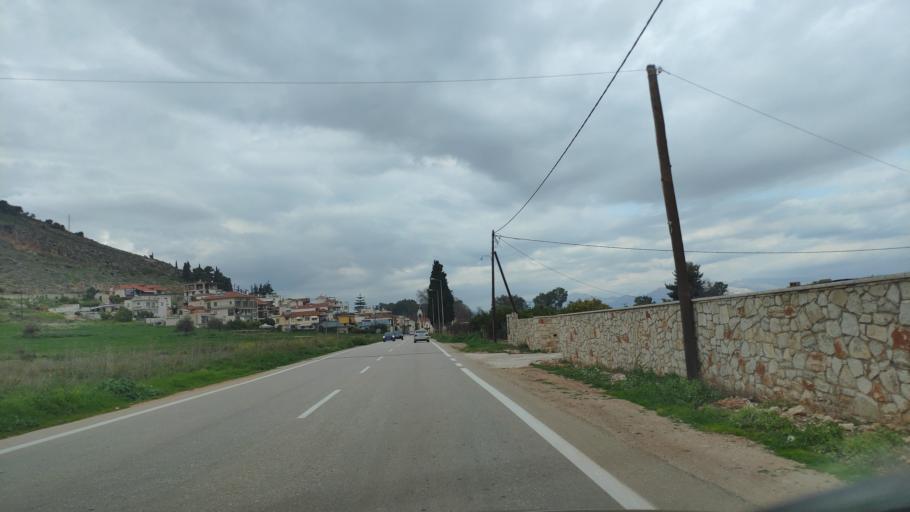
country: GR
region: Peloponnese
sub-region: Nomos Argolidos
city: Nea Kios
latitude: 37.5491
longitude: 22.7169
